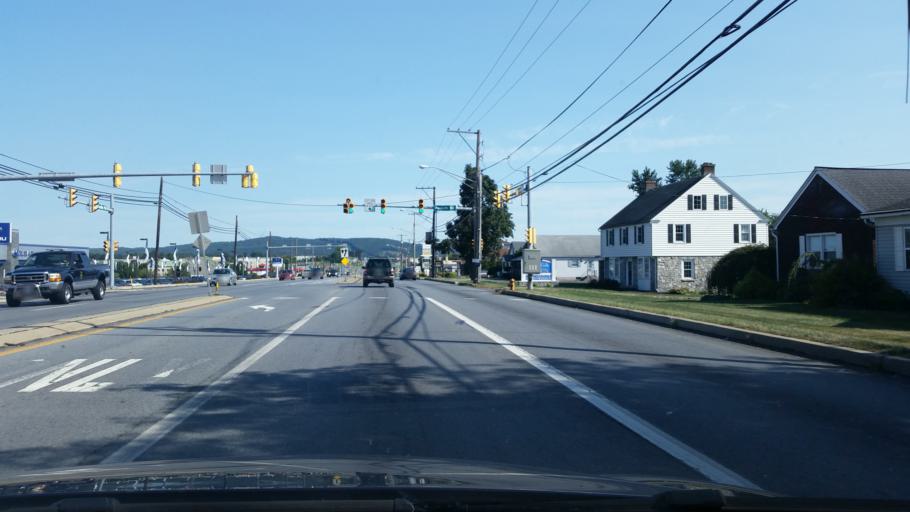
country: US
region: Pennsylvania
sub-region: Berks County
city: Leesport
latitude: 40.4474
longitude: -75.9615
